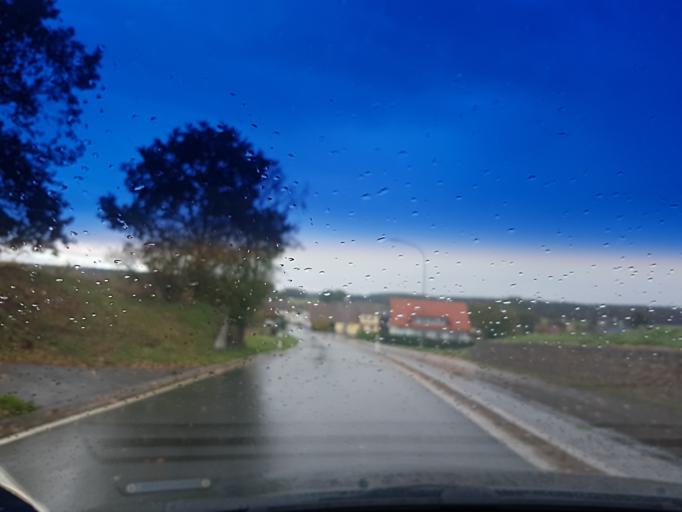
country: DE
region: Bavaria
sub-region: Regierungsbezirk Mittelfranken
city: Wachenroth
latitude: 49.7480
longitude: 10.6690
